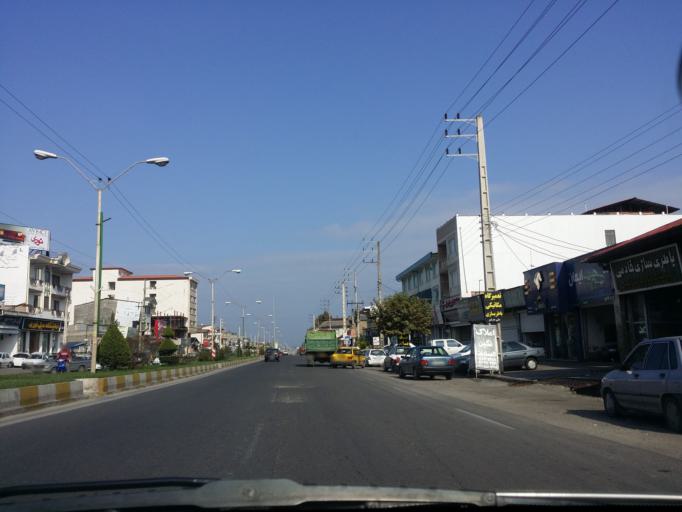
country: IR
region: Mazandaran
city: Chalus
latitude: 36.6680
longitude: 51.4092
